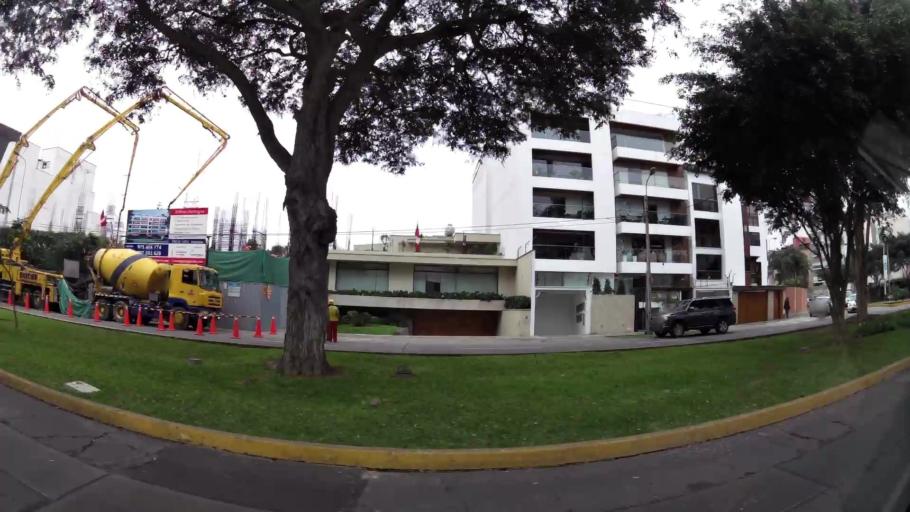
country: PE
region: Lima
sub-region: Lima
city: Surco
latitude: -12.1209
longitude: -77.0130
